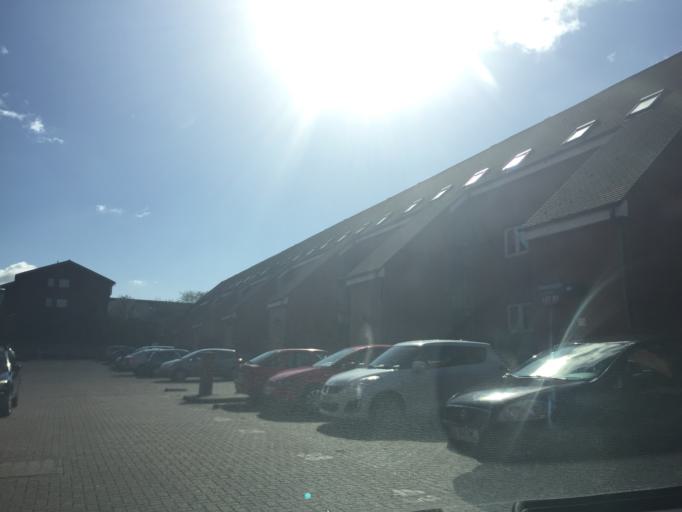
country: GB
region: England
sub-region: Essex
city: Harlow
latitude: 51.7735
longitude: 0.0964
